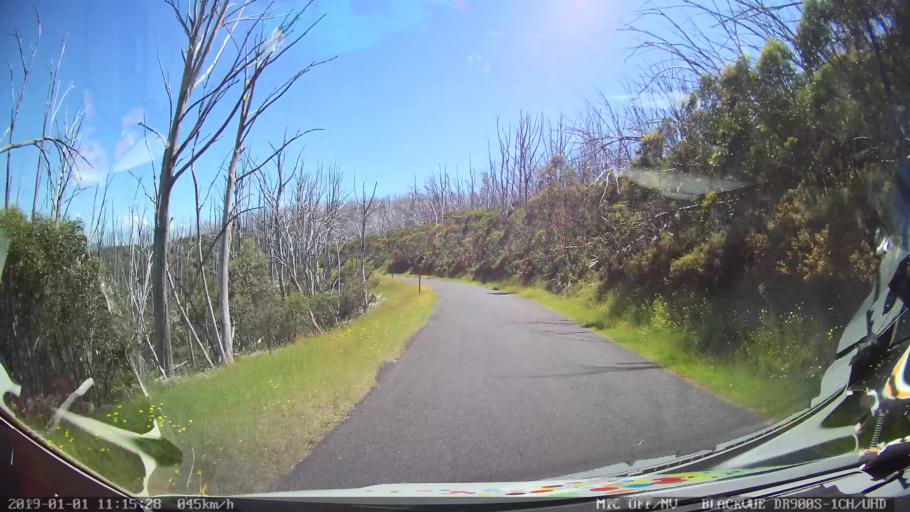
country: AU
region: New South Wales
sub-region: Snowy River
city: Jindabyne
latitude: -35.9449
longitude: 148.3871
